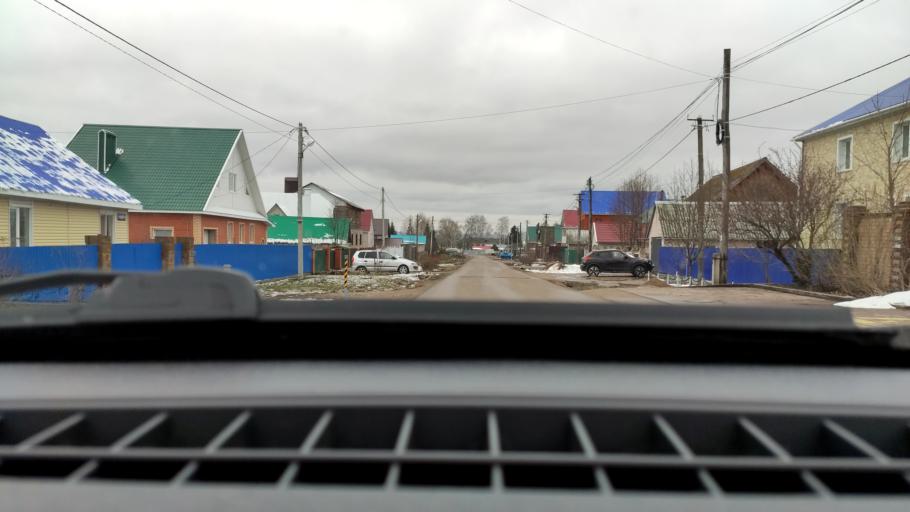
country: RU
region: Bashkortostan
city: Mikhaylovka
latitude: 54.8107
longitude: 55.8024
